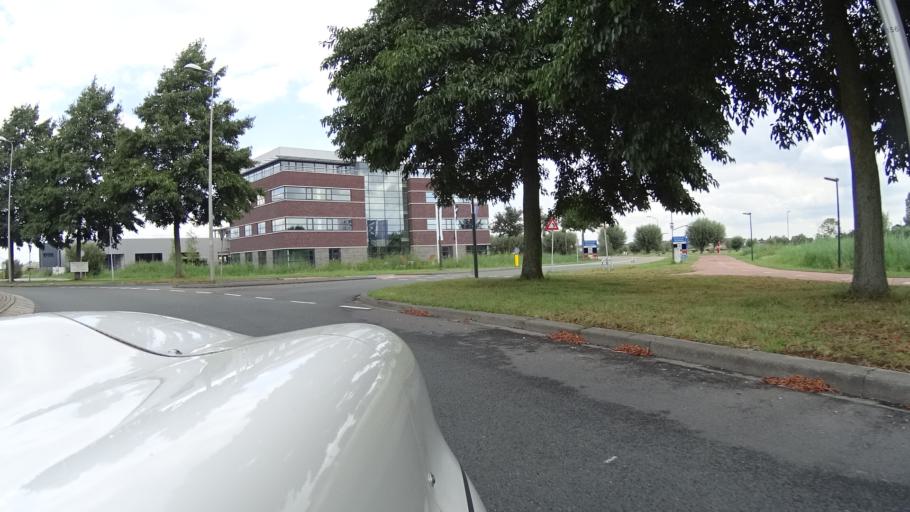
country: NL
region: South Holland
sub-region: Gemeente Sliedrecht
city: Sliedrecht
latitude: 51.8255
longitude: 4.8049
